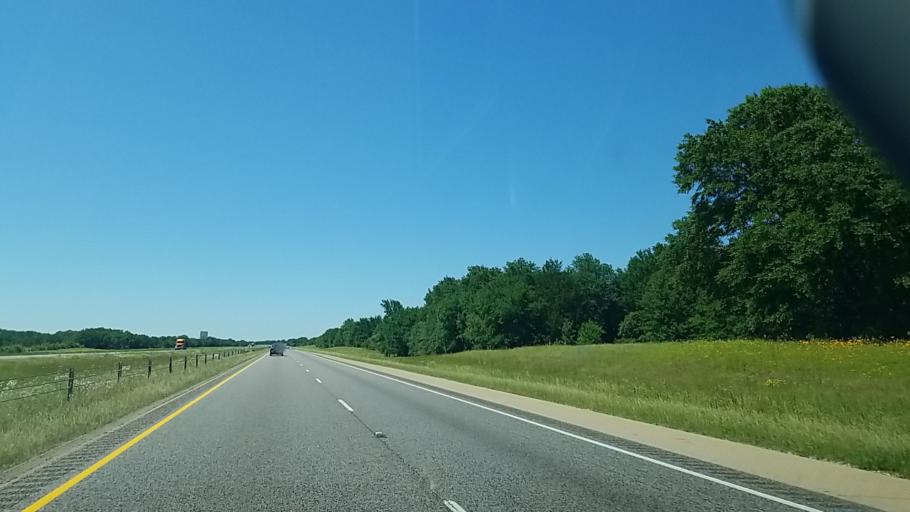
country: US
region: Texas
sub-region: Freestone County
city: Fairfield
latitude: 31.6726
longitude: -96.1635
